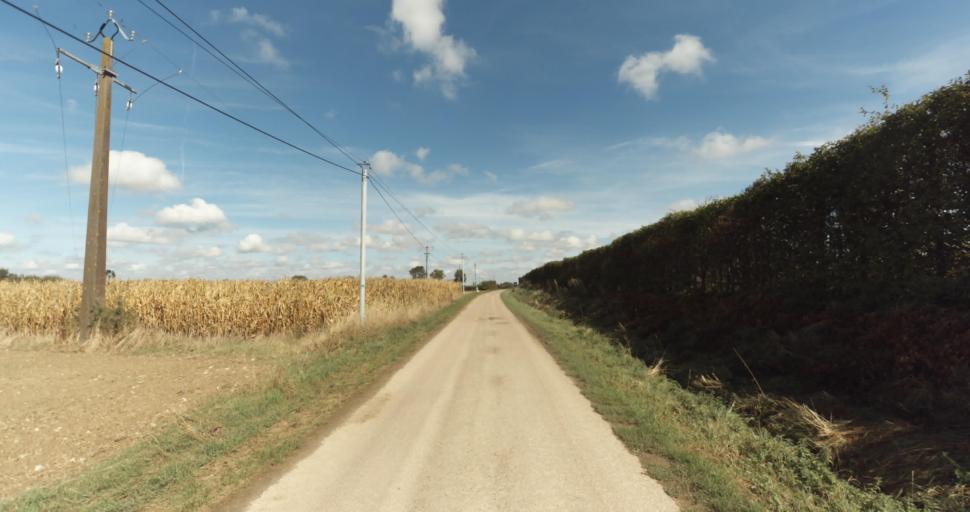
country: FR
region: Lower Normandy
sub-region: Departement du Calvados
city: Orbec
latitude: 48.9615
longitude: 0.4051
